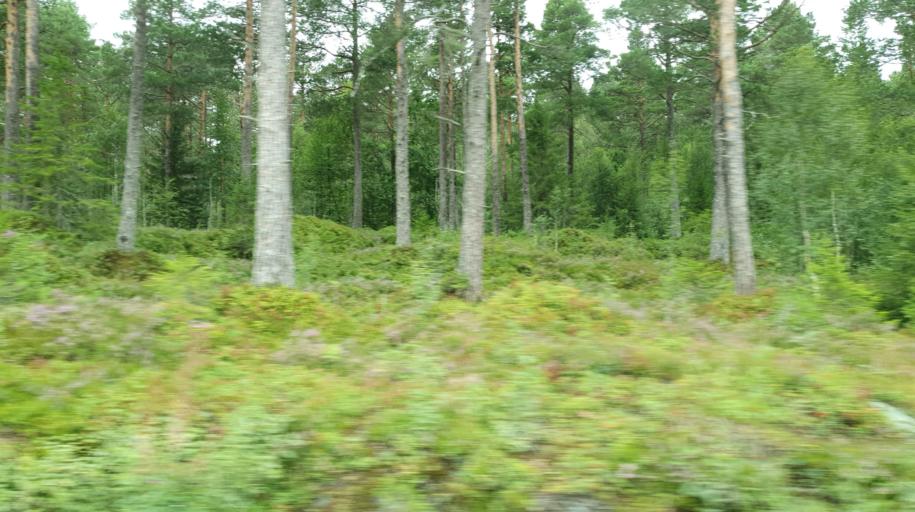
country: NO
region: Nord-Trondelag
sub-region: Stjordal
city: Stjordalshalsen
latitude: 63.4005
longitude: 10.9704
